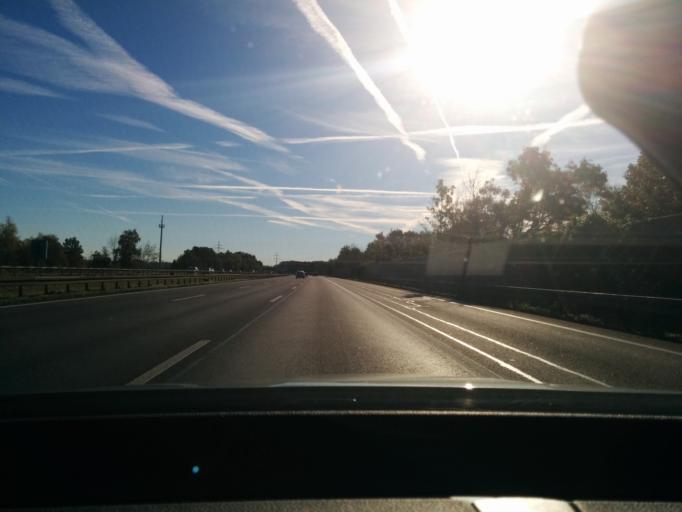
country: DE
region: Bavaria
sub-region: Upper Bavaria
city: Unterfoehring
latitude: 48.2020
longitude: 11.6619
